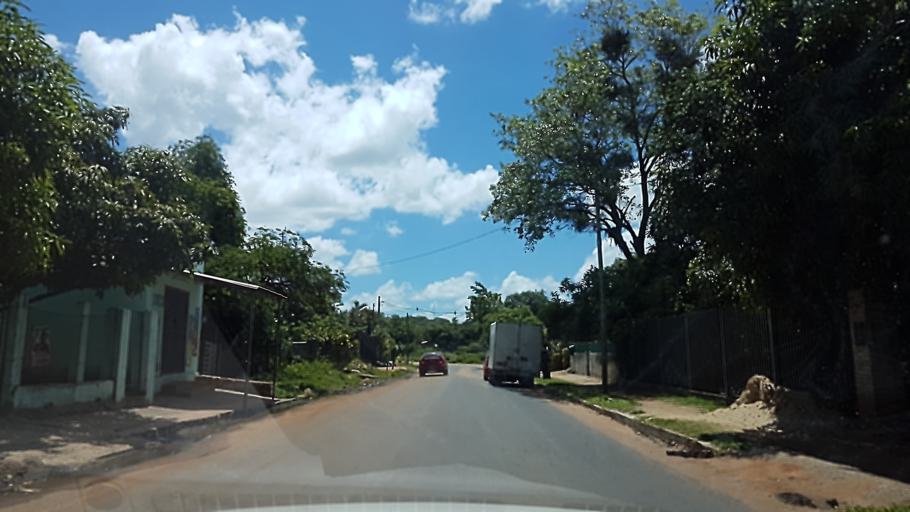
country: PY
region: Central
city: Colonia Mariano Roque Alonso
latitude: -25.2372
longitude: -57.5282
